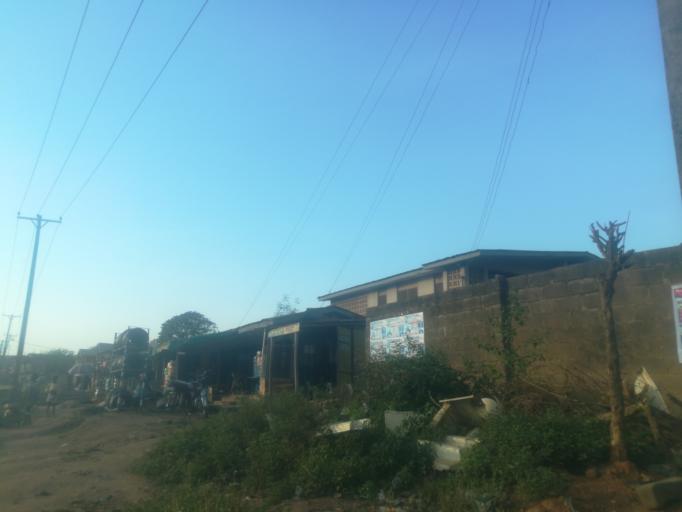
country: NG
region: Oyo
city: Moniya
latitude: 7.5348
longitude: 3.9057
